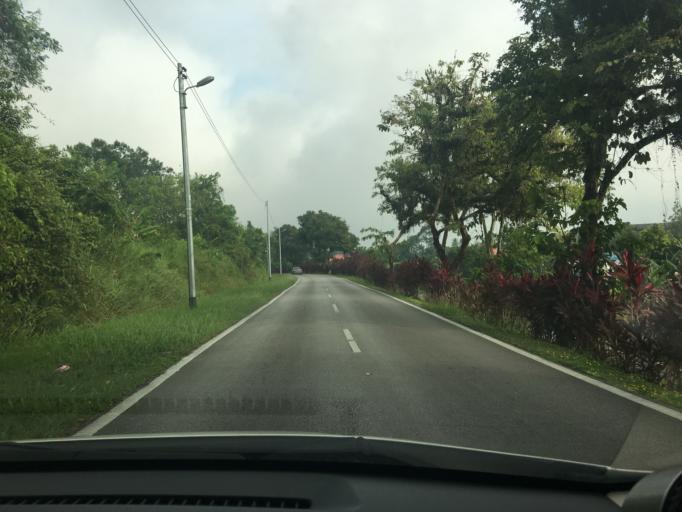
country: MY
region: Sarawak
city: Kuching
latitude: 1.4114
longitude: 110.1581
